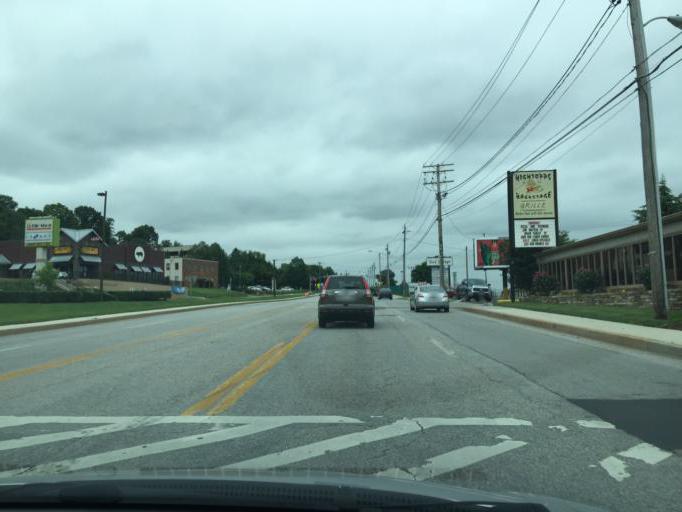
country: US
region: Maryland
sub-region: Baltimore County
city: Timonium
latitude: 39.4495
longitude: -76.6302
